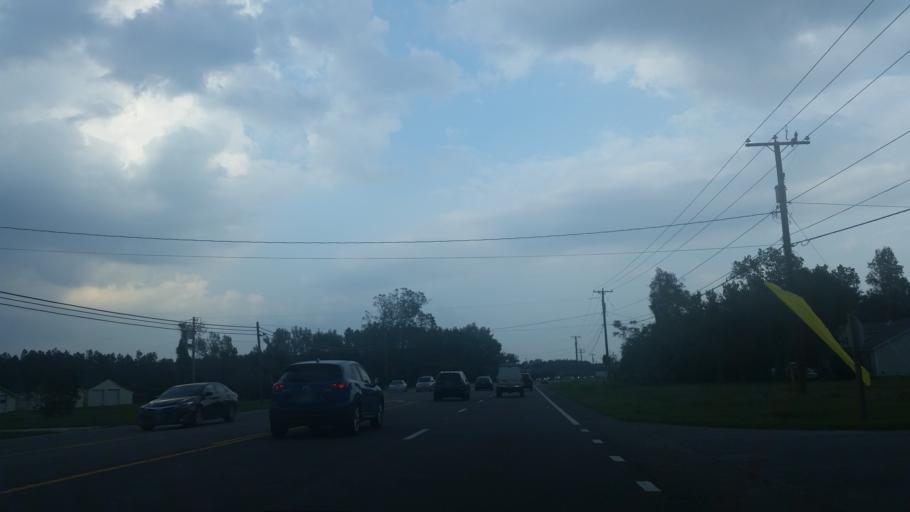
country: US
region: North Carolina
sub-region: Dare County
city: Southern Shores
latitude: 36.1411
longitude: -75.8427
